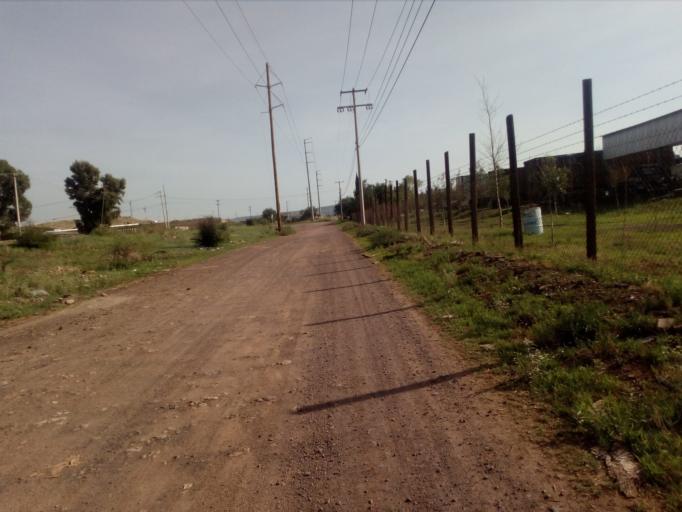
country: MX
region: Durango
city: Victoria de Durango
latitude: 24.0610
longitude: -104.6537
